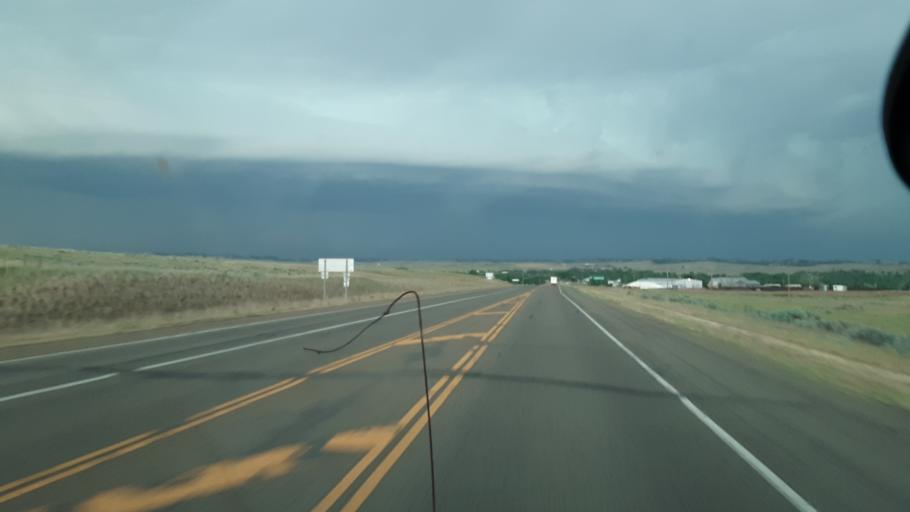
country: US
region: Montana
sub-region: Powder River County
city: Broadus
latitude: 45.4232
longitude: -105.3973
